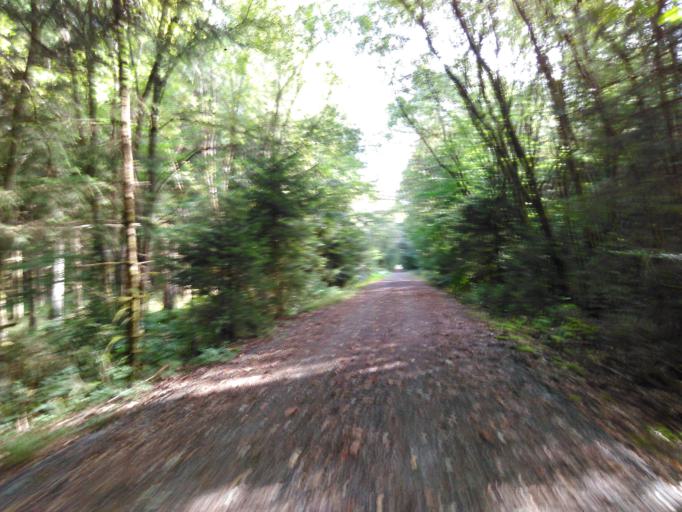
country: BE
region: Wallonia
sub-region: Province du Luxembourg
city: Vaux-sur-Sure
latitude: 49.9366
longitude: 5.5529
